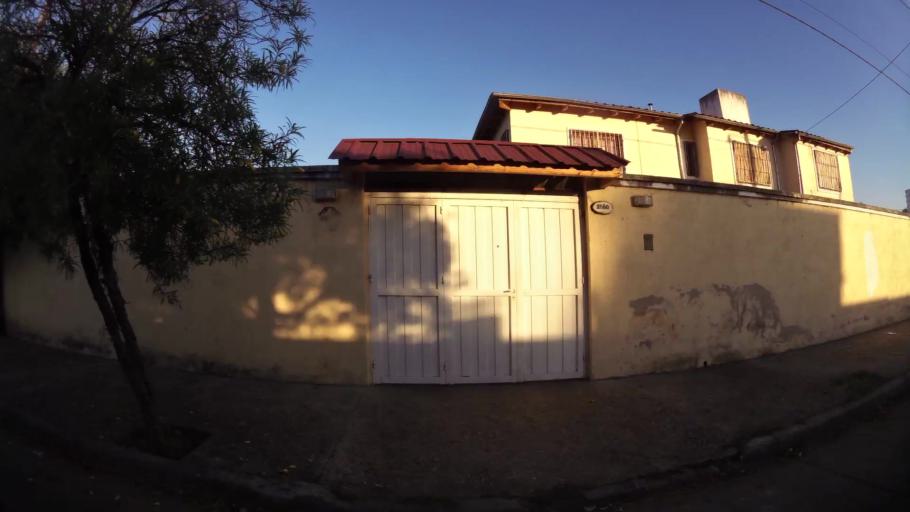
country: AR
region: Cordoba
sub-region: Departamento de Capital
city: Cordoba
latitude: -31.3796
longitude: -64.2084
